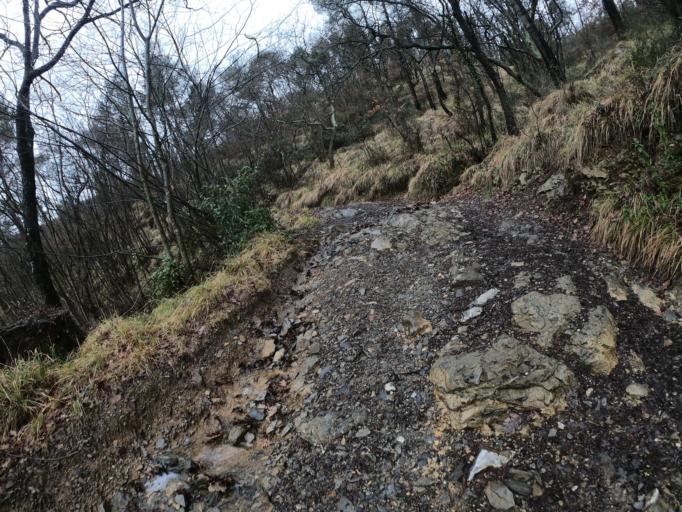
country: IT
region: Liguria
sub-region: Provincia di Imperia
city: Villa Faraldi
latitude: 43.9780
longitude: 8.1042
